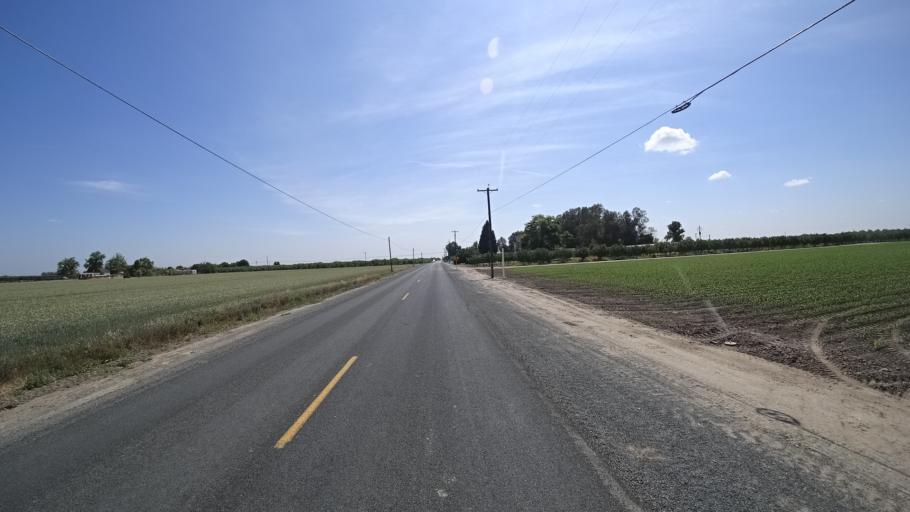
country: US
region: California
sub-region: Kings County
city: Armona
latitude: 36.2693
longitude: -119.7118
